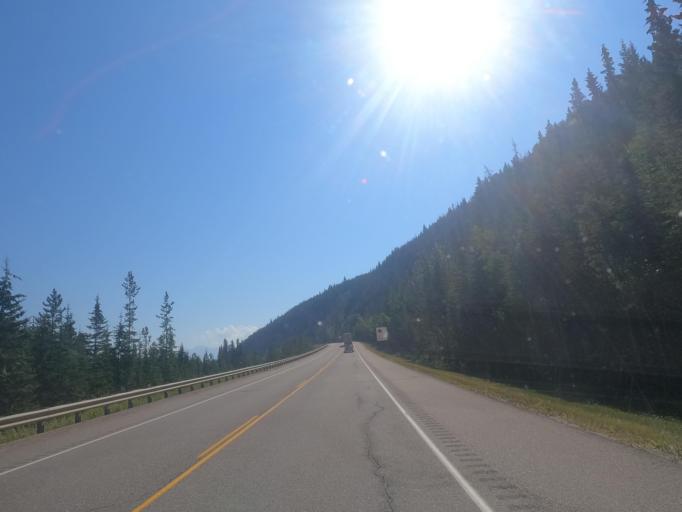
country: CA
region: Alberta
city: Jasper Park Lodge
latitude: 52.8782
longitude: -118.3451
